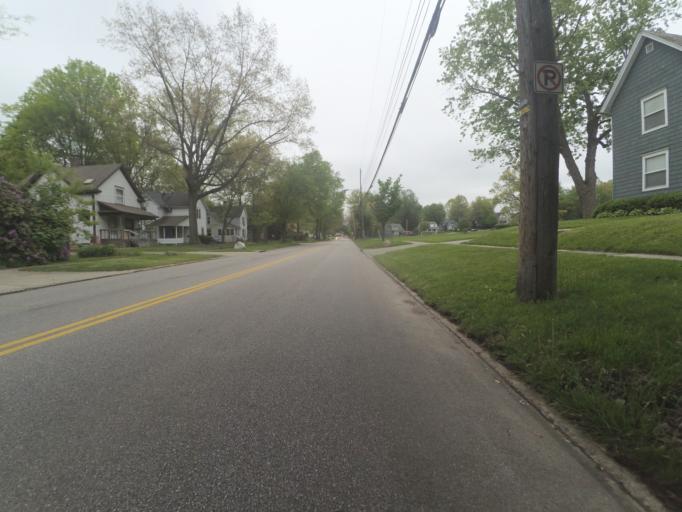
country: US
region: Ohio
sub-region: Portage County
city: Kent
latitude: 41.1578
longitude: -81.3555
